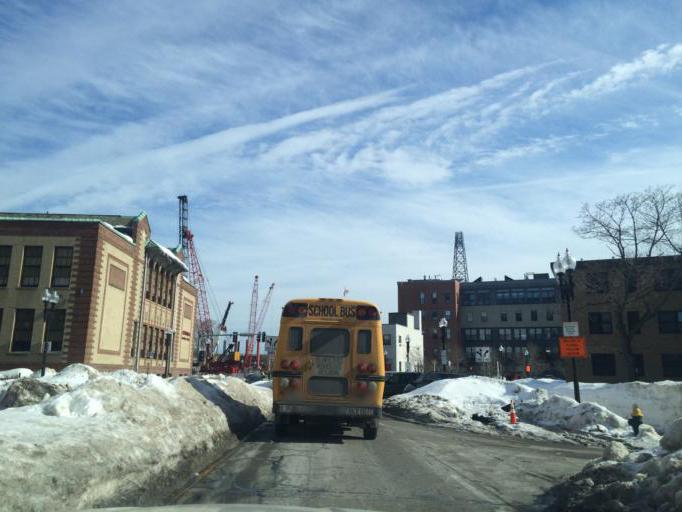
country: US
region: Massachusetts
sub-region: Suffolk County
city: Boston
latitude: 42.3404
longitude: -71.0696
